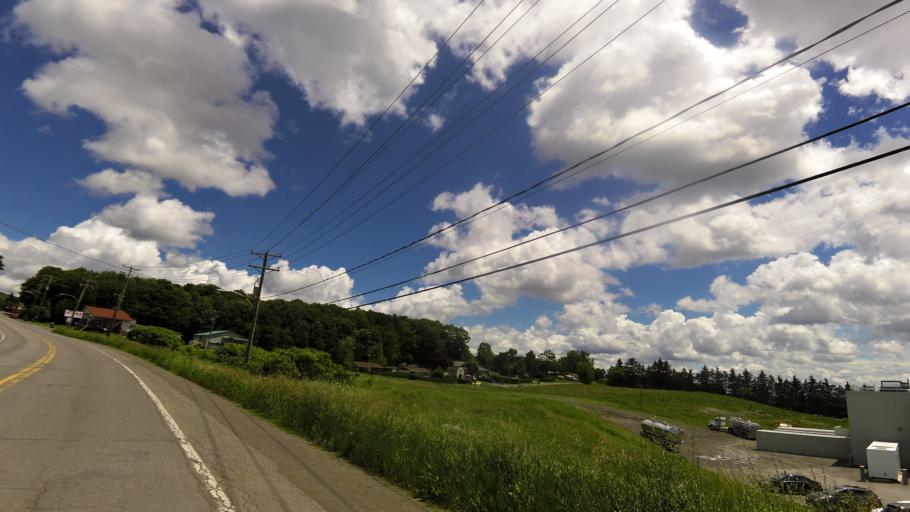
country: CA
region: Quebec
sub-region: Laurentides
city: Oka
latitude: 45.4956
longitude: -74.0278
